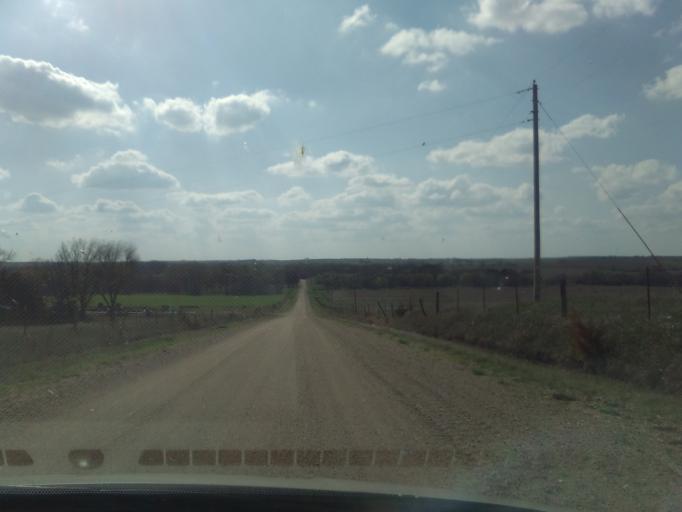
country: US
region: Nebraska
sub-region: Webster County
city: Red Cloud
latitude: 40.0313
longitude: -98.4504
